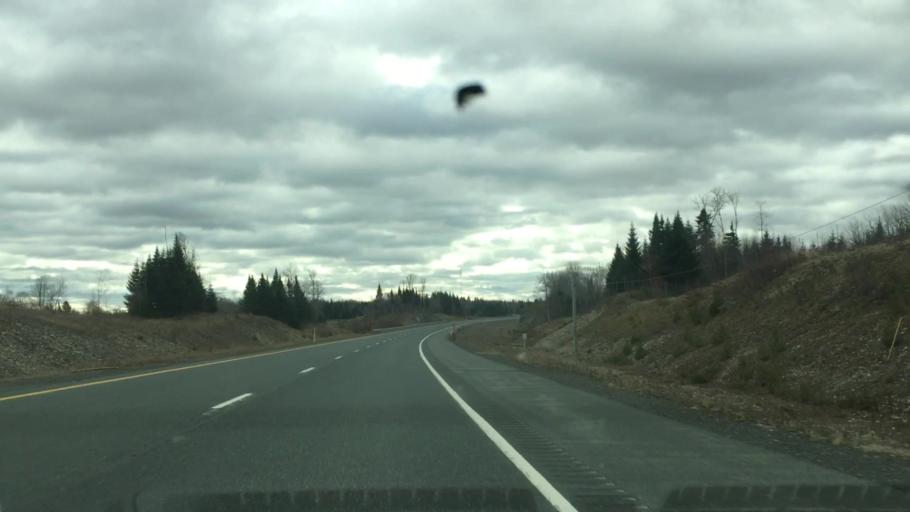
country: US
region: Maine
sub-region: Aroostook County
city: Easton
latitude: 46.6240
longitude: -67.7392
